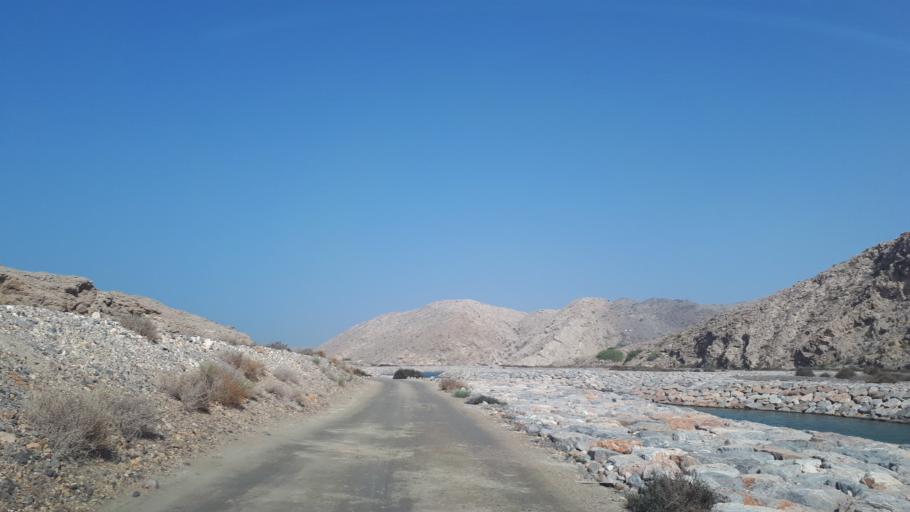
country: OM
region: Muhafazat Masqat
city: Muscat
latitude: 23.5392
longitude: 58.6602
